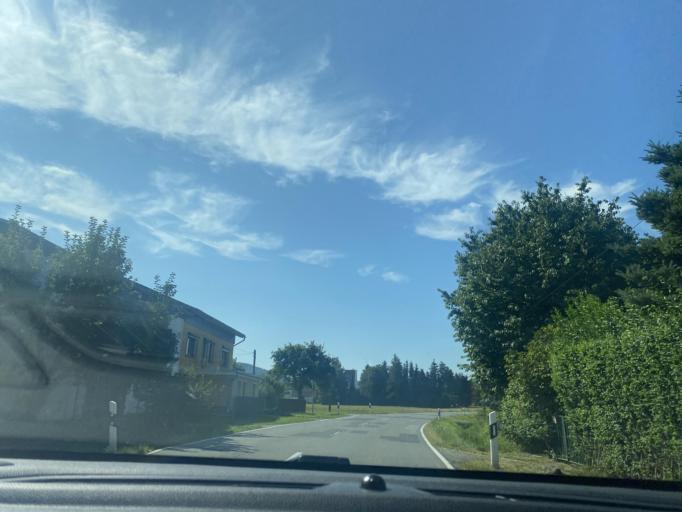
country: DE
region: Saxony
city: Grosshennersdorf
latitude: 50.9984
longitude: 14.7943
